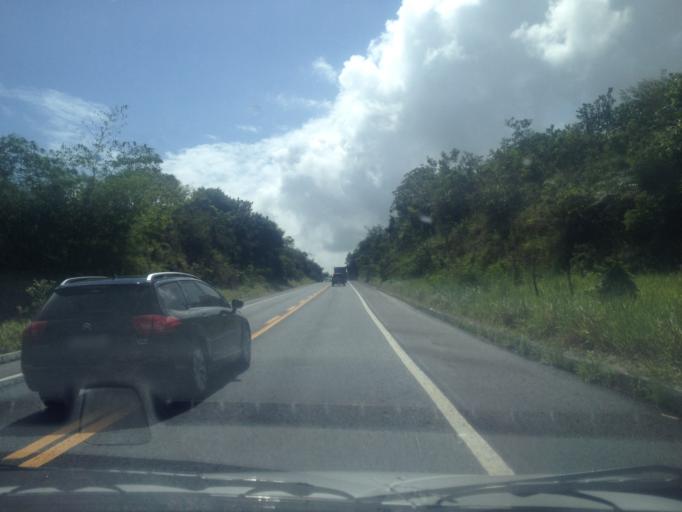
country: BR
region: Sergipe
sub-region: Indiaroba
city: Indiaroba
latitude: -11.6095
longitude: -37.5388
